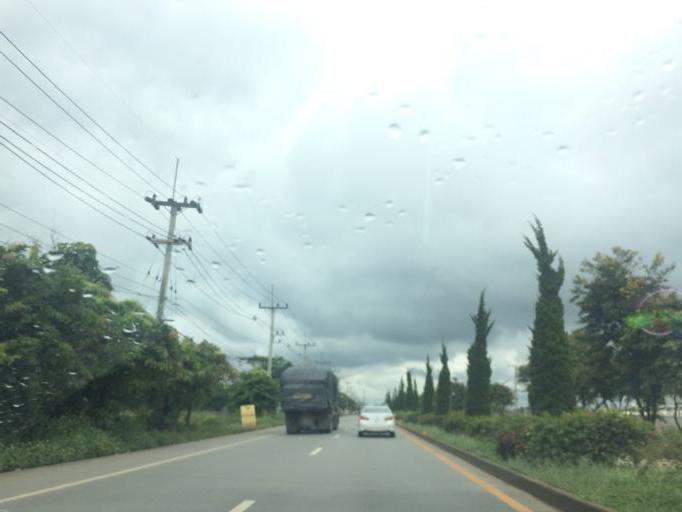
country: TH
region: Chiang Rai
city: Mae Chan
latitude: 20.0298
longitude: 99.8736
